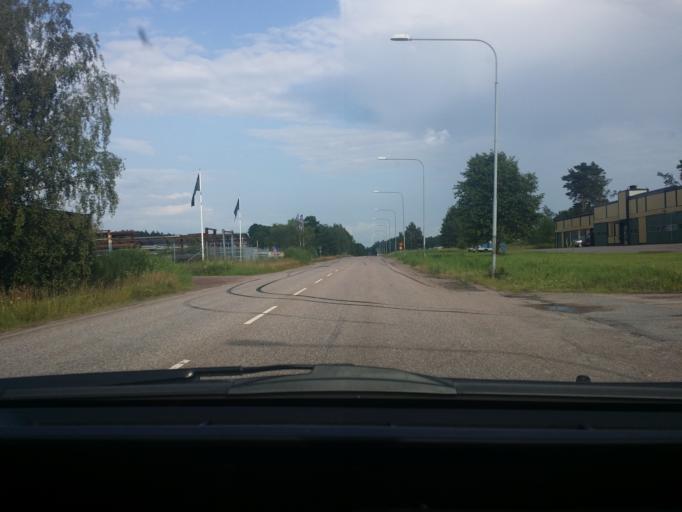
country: SE
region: Vaestmanland
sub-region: Hallstahammars Kommun
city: Kolback
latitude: 59.5644
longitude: 16.2430
